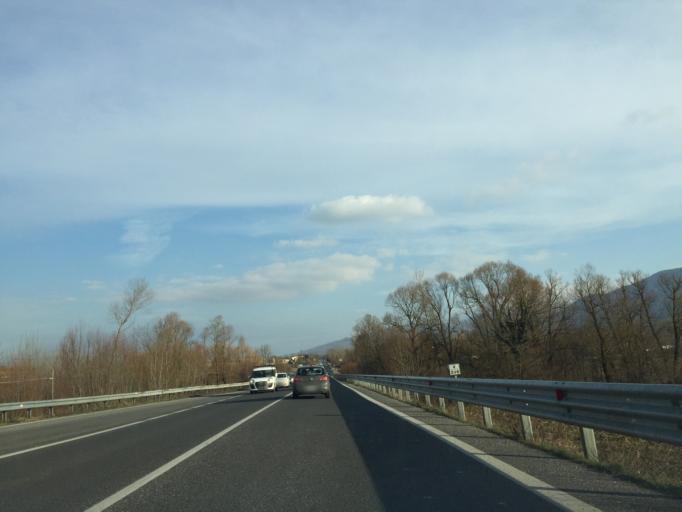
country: IT
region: Molise
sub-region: Provincia di Campobasso
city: Bojano
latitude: 41.4840
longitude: 14.4927
